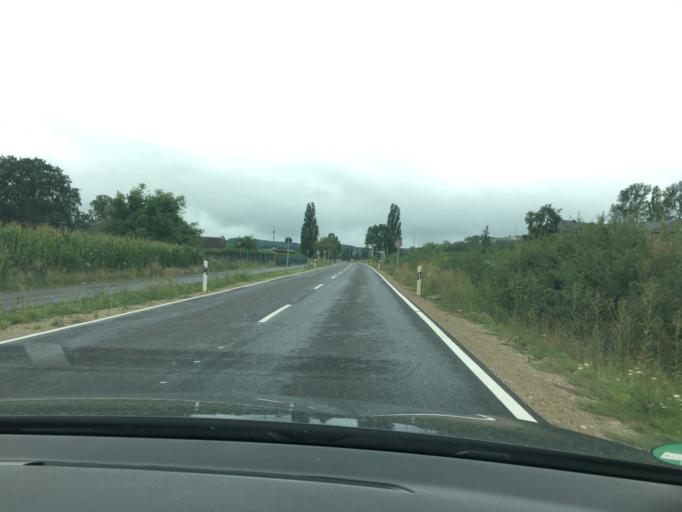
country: DE
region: North Rhine-Westphalia
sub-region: Regierungsbezirk Koln
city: Kreuzau
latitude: 50.7543
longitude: 6.4622
